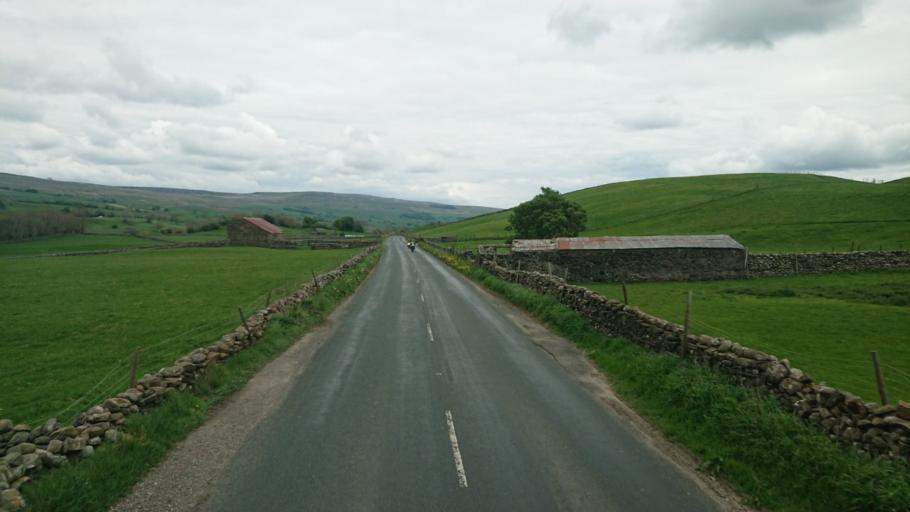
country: GB
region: England
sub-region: County Durham
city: Bowes
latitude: 54.3041
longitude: -2.1322
